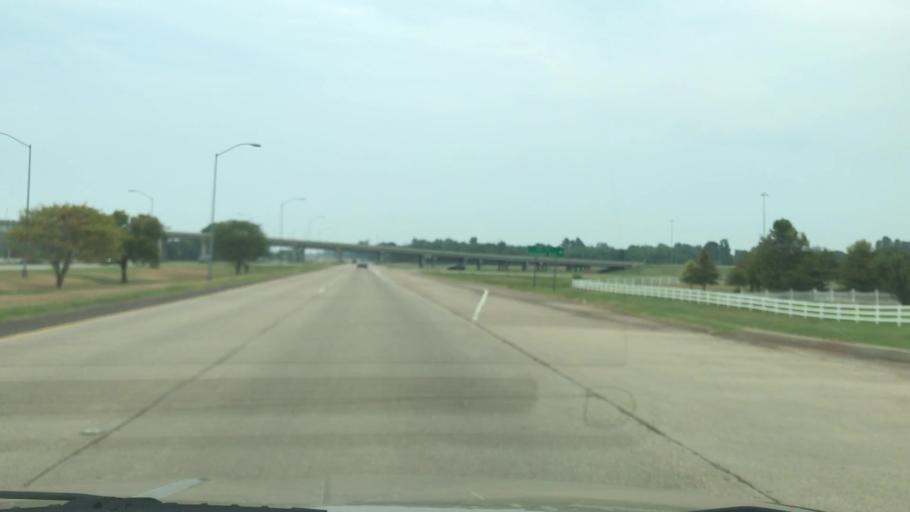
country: US
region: Louisiana
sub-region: Bossier Parish
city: Bossier City
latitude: 32.4919
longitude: -93.6934
